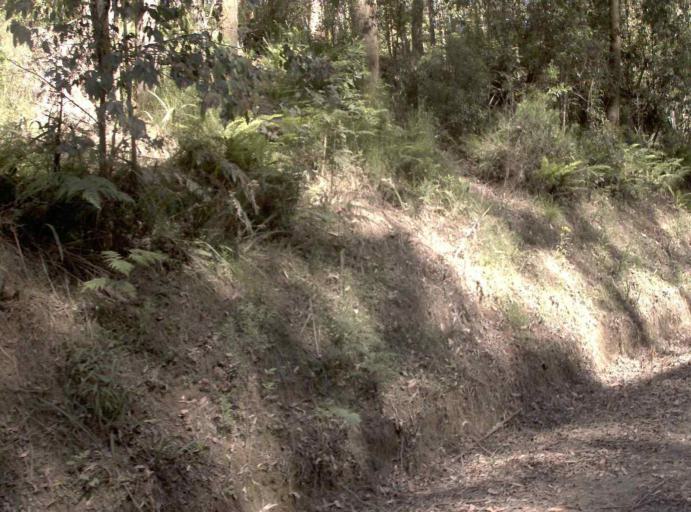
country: AU
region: New South Wales
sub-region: Bombala
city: Bombala
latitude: -37.2141
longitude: 148.7457
